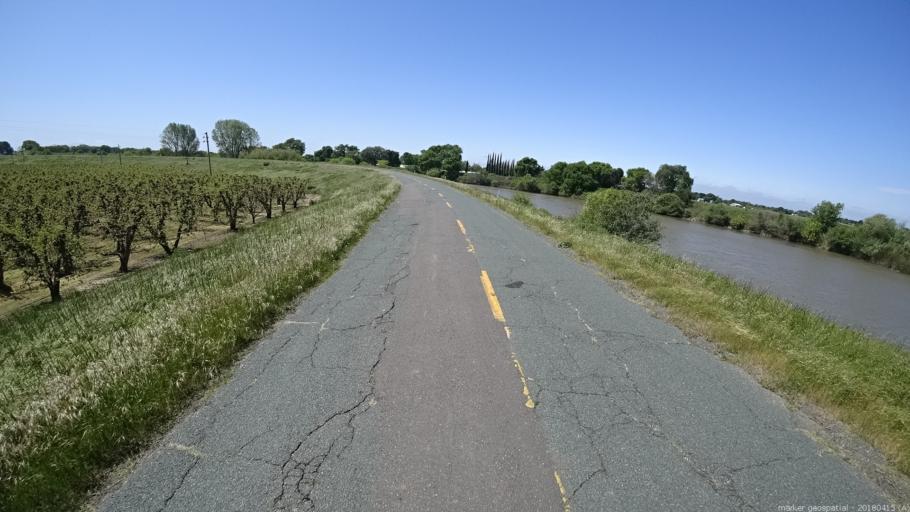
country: US
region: California
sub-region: Sacramento County
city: Walnut Grove
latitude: 38.2617
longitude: -121.5922
